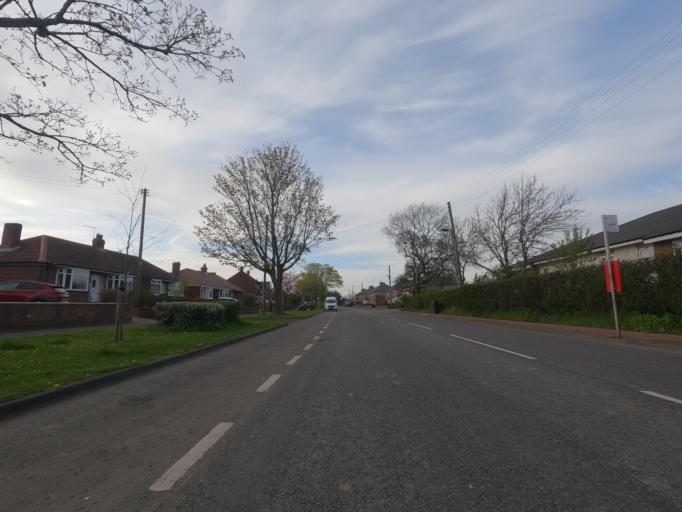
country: GB
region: England
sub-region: Newcastle upon Tyne
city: Dinnington
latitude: 55.0510
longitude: -1.6726
